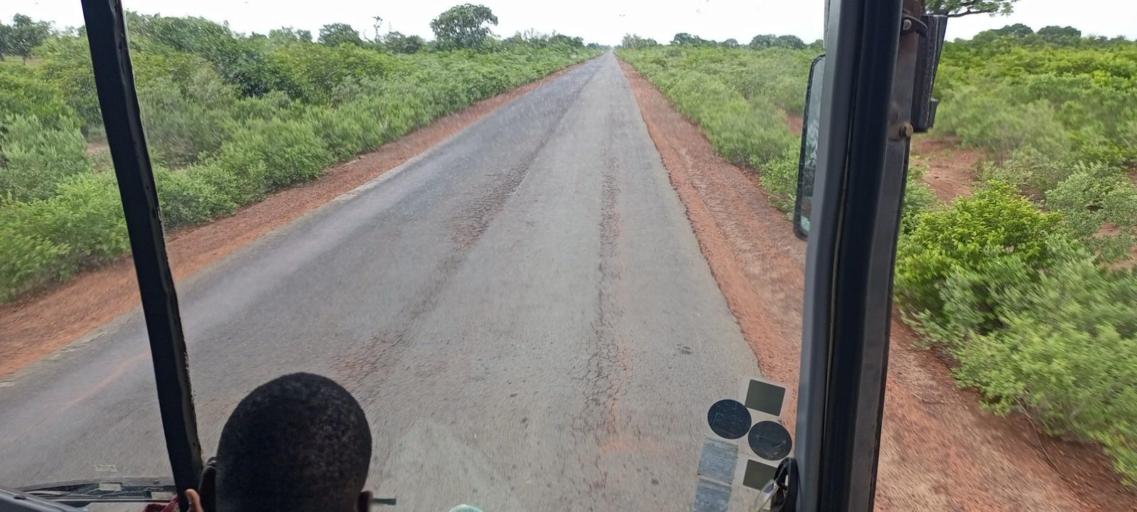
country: ML
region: Sikasso
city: Koutiala
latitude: 12.5609
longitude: -5.5933
